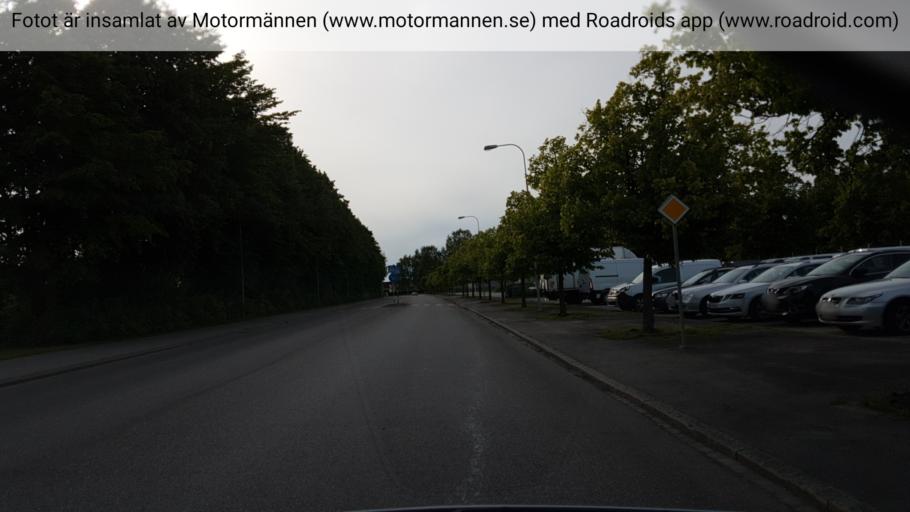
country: SE
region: Vaestra Goetaland
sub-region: Lidkopings Kommun
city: Lidkoping
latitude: 58.4969
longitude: 13.1463
